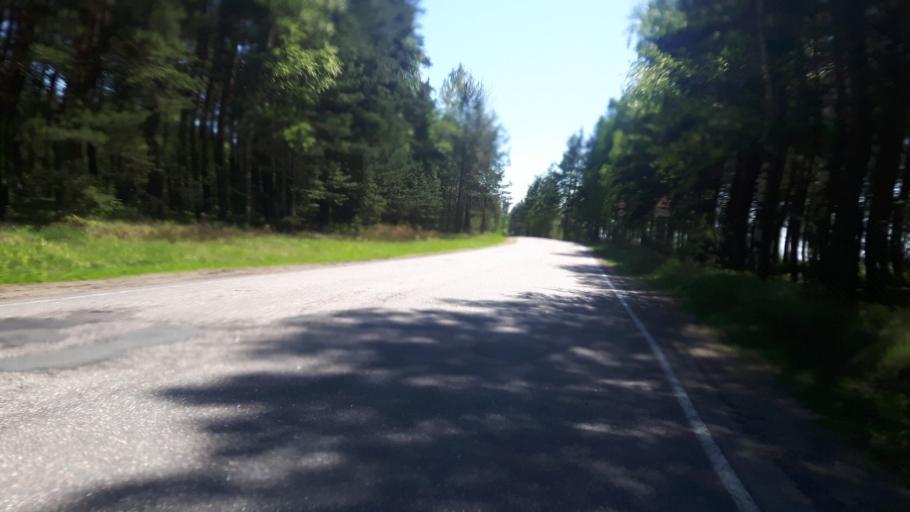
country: RU
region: Leningrad
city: Glebychevo
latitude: 60.3281
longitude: 28.8234
